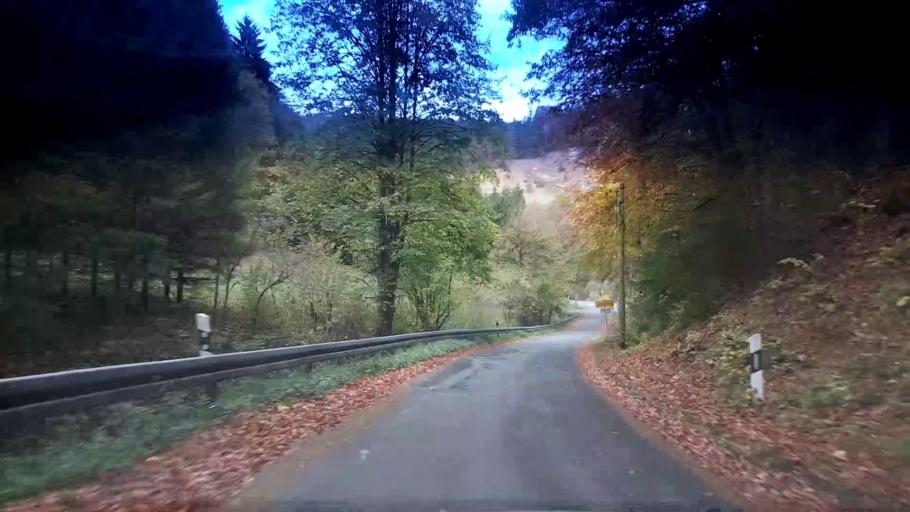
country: DE
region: Bavaria
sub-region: Upper Franconia
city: Wattendorf
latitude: 50.0254
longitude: 11.1038
